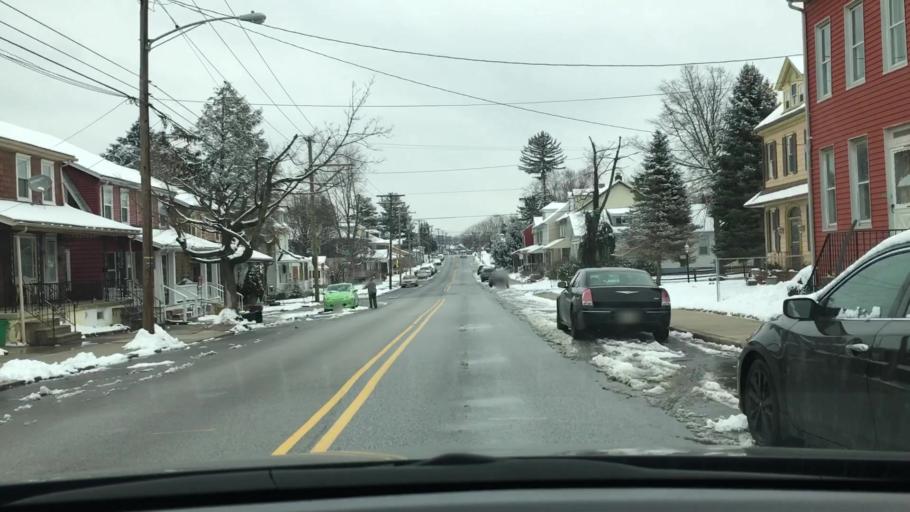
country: US
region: Pennsylvania
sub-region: York County
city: Valley View
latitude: 39.9579
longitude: -76.7111
